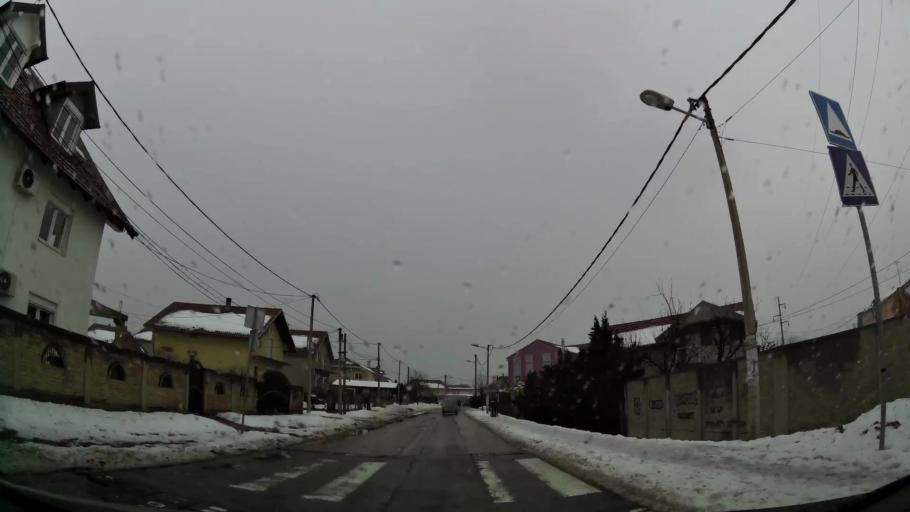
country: RS
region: Central Serbia
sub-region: Belgrade
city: Zemun
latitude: 44.8469
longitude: 20.3564
